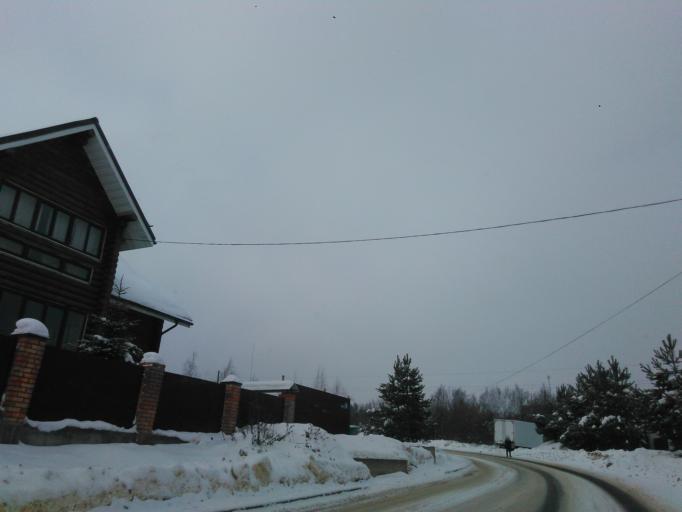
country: RU
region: Moskovskaya
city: Yakhroma
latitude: 56.2750
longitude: 37.4847
